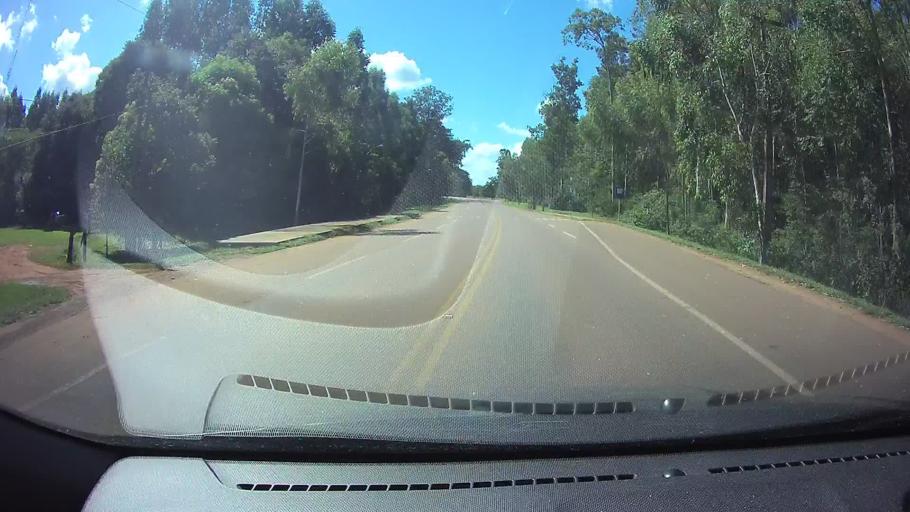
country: PY
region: Guaira
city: Coronel Martinez
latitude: -25.7690
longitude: -56.6524
